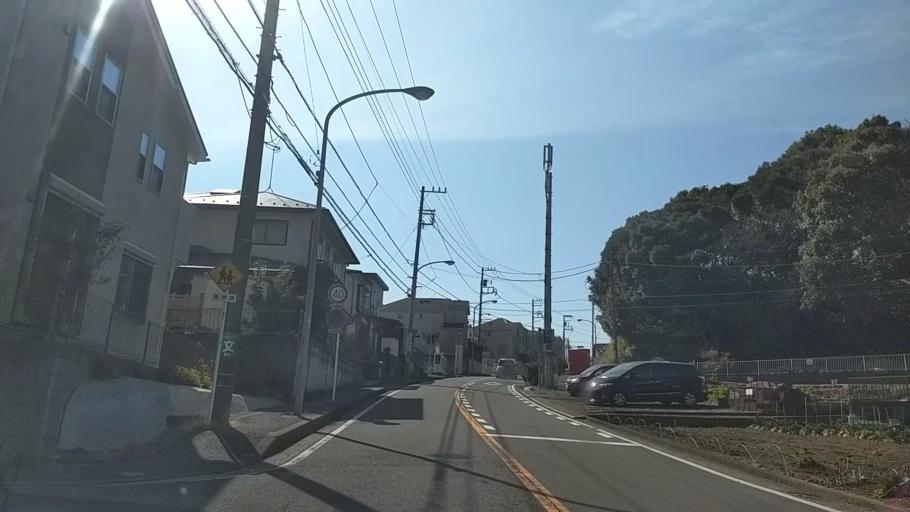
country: JP
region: Kanagawa
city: Kamakura
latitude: 35.3971
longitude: 139.5564
